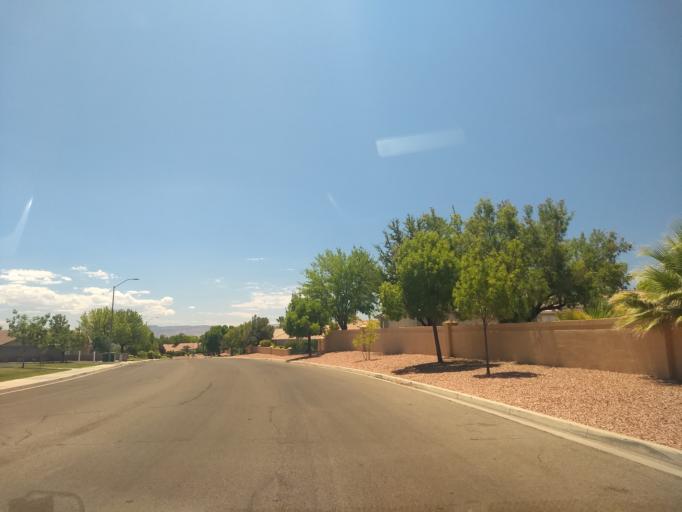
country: US
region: Utah
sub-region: Washington County
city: Washington
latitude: 37.1430
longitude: -113.5238
